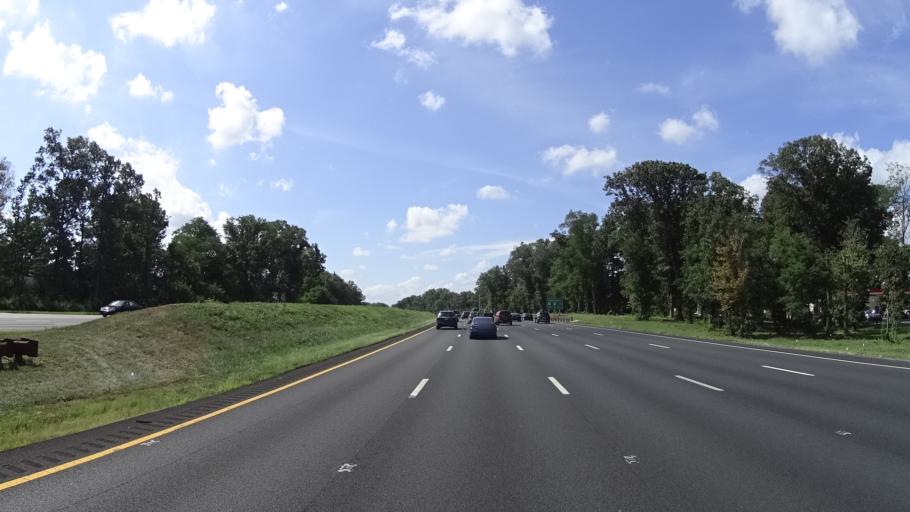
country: US
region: New Jersey
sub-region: Middlesex County
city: Iselin
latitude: 40.5825
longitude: -74.3304
